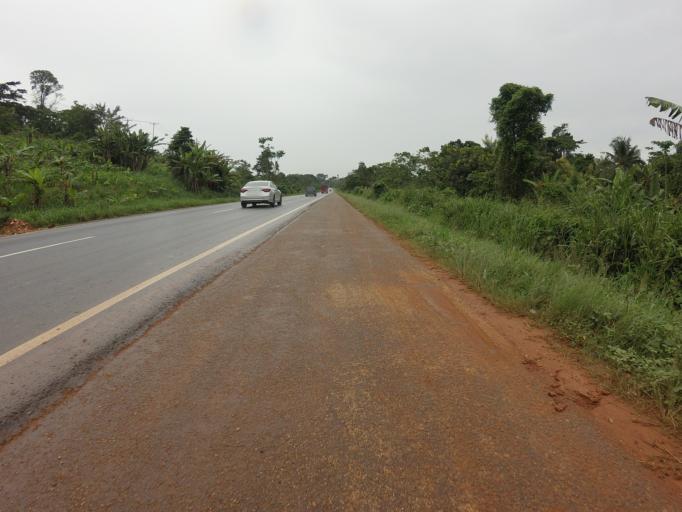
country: GH
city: Kibi
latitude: 6.1433
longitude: -0.4893
